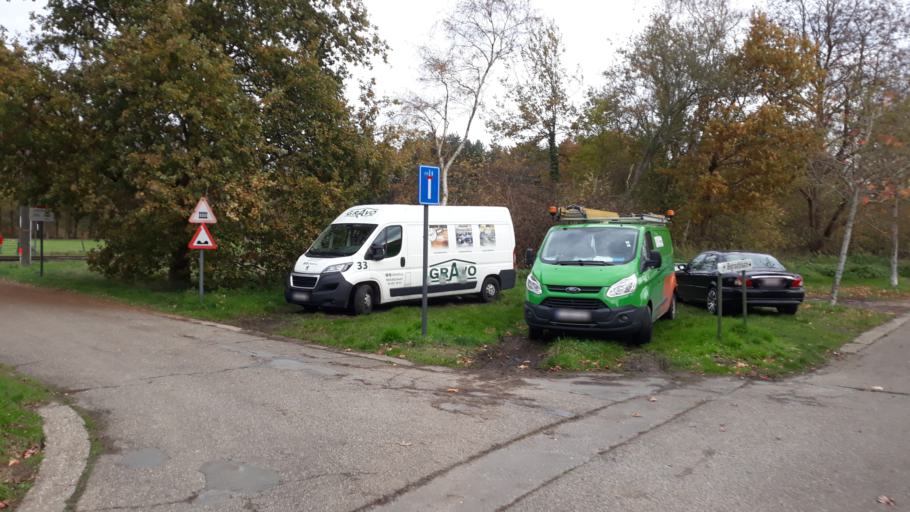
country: BE
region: Flanders
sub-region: Provincie Antwerpen
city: Herenthout
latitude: 51.1660
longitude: 4.7556
